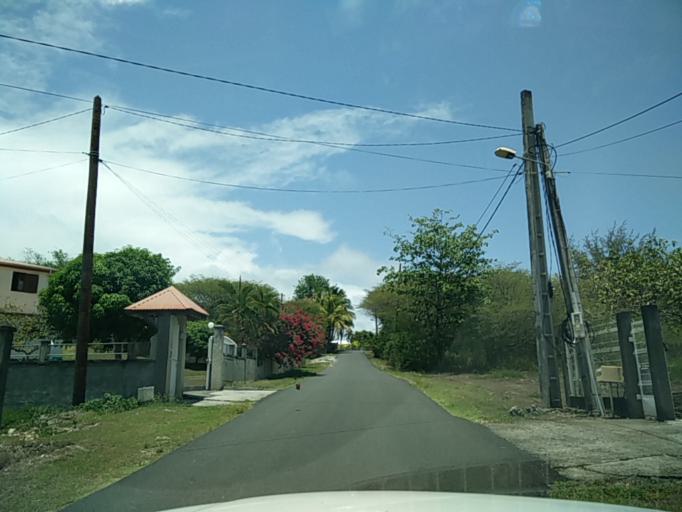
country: GP
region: Guadeloupe
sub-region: Guadeloupe
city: Sainte-Anne
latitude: 16.2195
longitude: -61.4045
